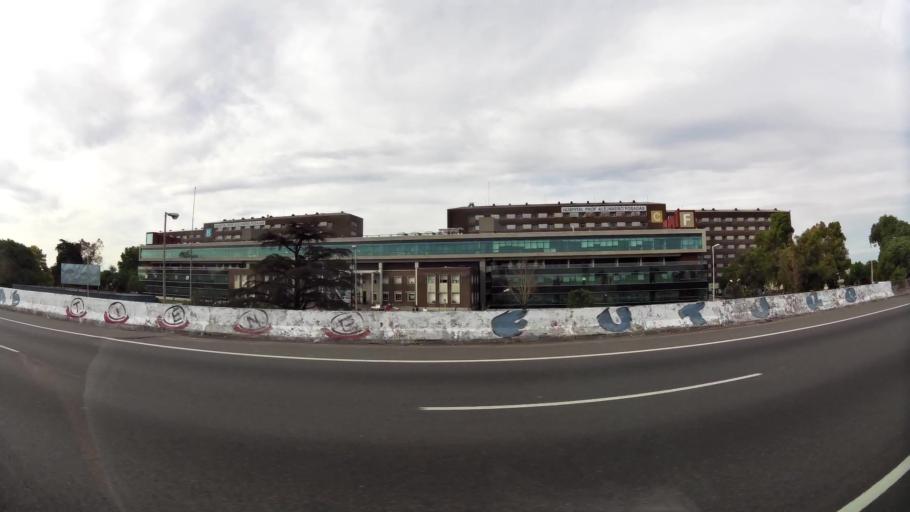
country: AR
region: Buenos Aires
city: Caseros
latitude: -34.6312
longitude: -58.5751
